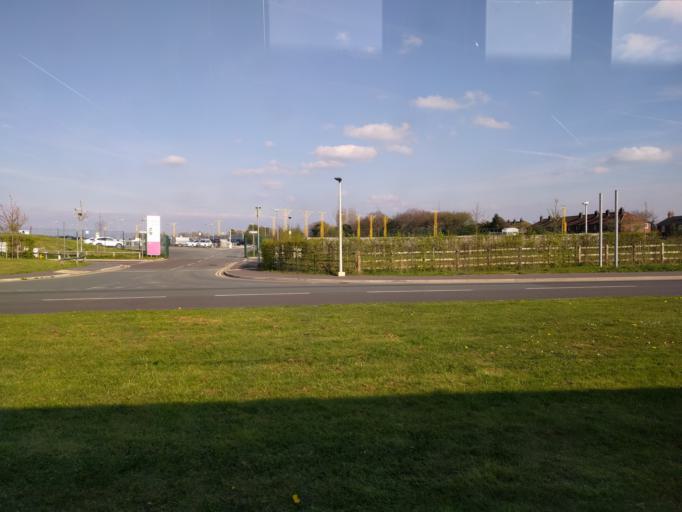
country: GB
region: England
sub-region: Manchester
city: Ringway
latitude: 53.3659
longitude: -2.2527
